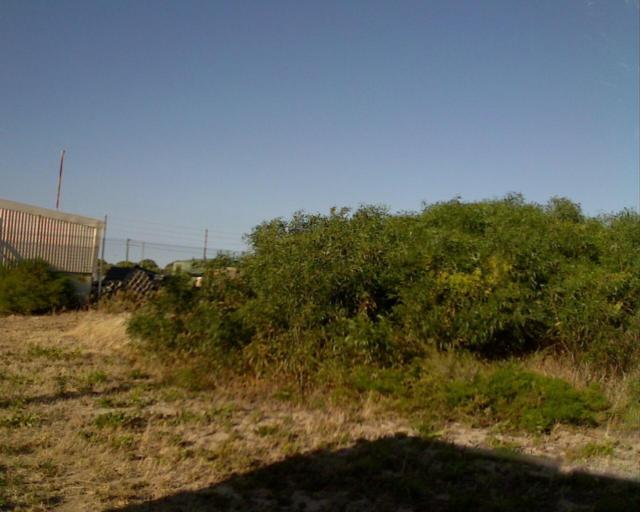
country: AU
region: Western Australia
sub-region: Dandaragan
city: Jurien Bay
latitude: -30.0529
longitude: 114.9790
